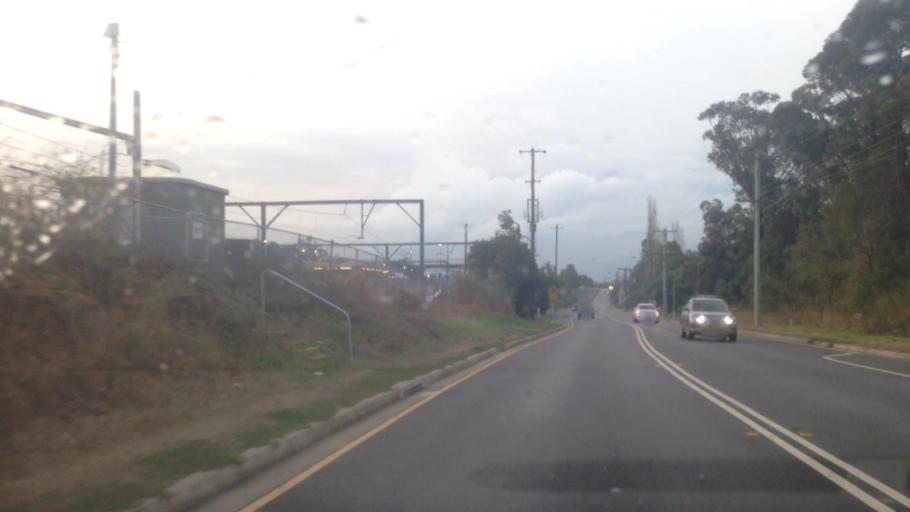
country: AU
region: New South Wales
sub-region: Wyong Shire
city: Charmhaven
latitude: -33.1815
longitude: 151.4875
